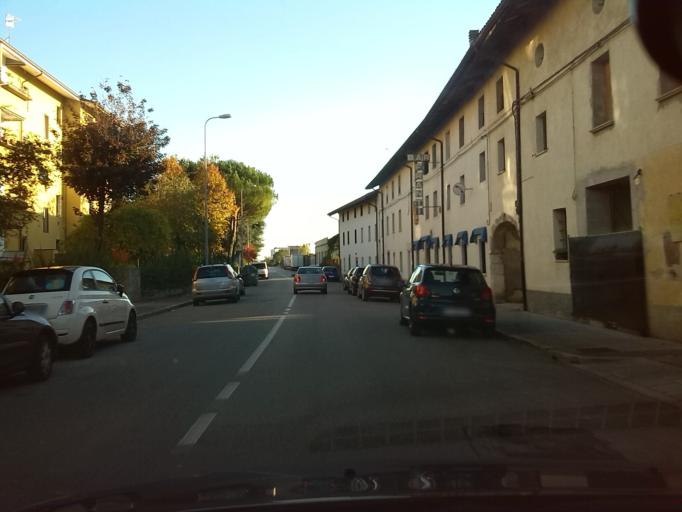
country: IT
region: Friuli Venezia Giulia
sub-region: Provincia di Udine
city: Udine
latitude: 46.0546
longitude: 13.2202
